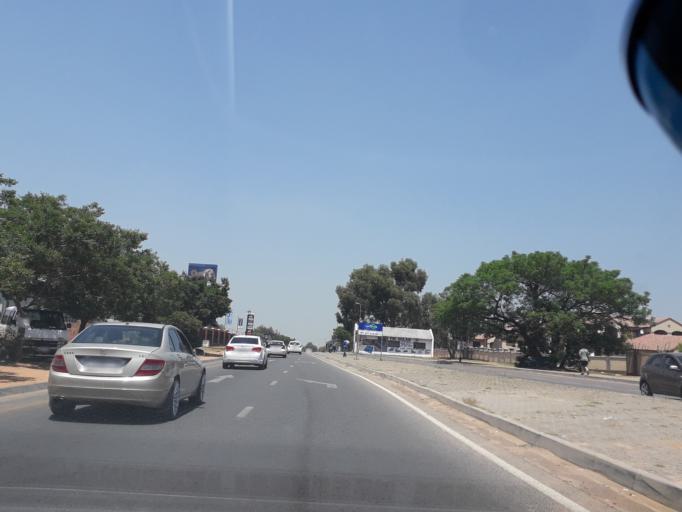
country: ZA
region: Gauteng
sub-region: City of Johannesburg Metropolitan Municipality
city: Midrand
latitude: -25.9804
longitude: 28.1179
